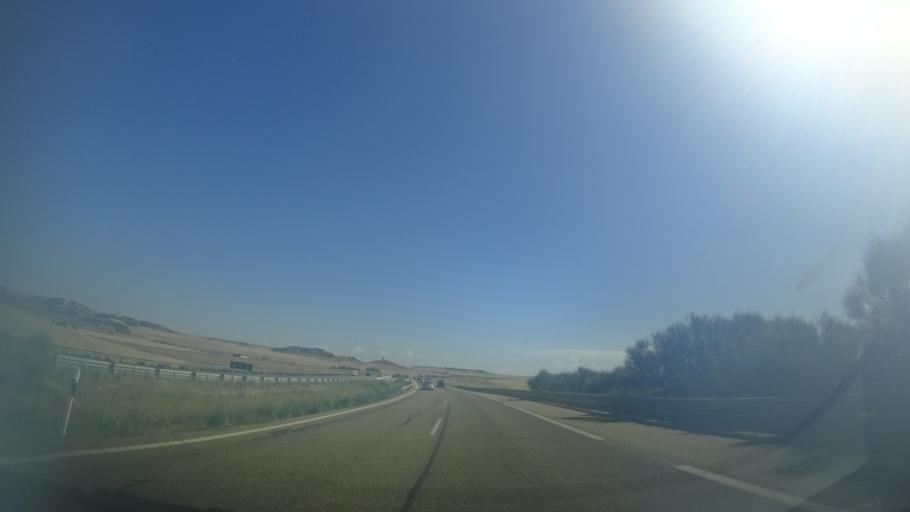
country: ES
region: Castille and Leon
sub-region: Provincia de Valladolid
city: Mota del Marques
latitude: 41.6628
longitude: -5.1978
